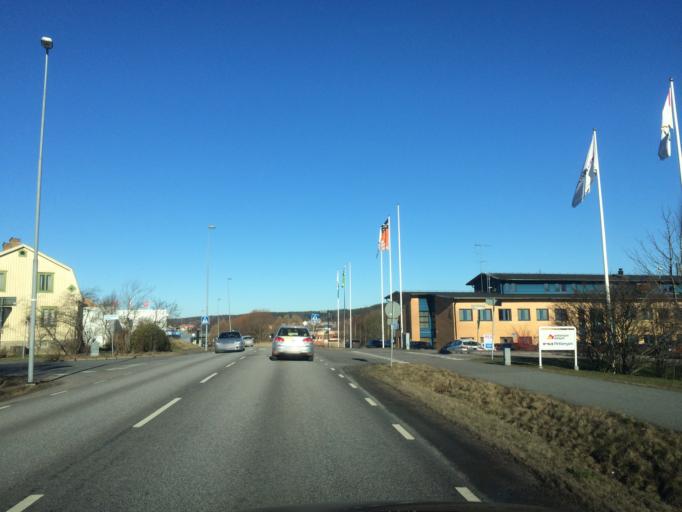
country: SE
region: Vaestra Goetaland
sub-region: Molndal
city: Moelndal
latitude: 57.6421
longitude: 11.9914
